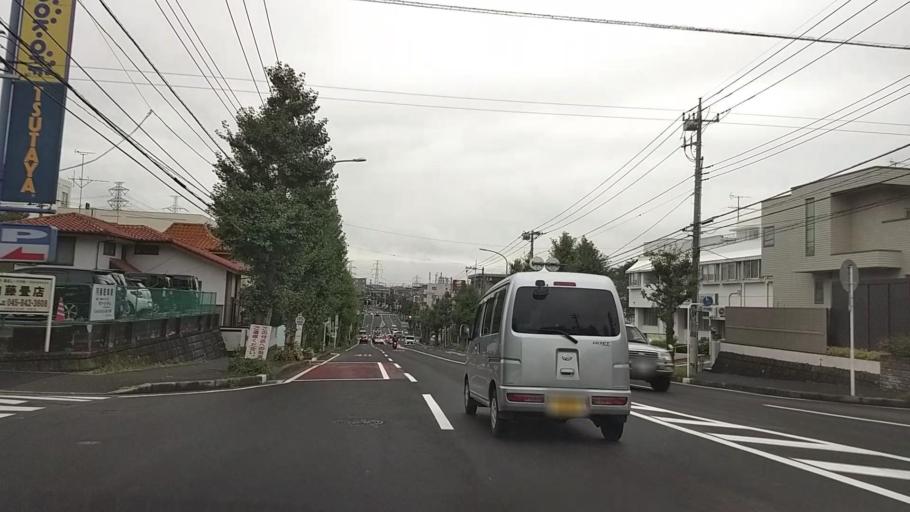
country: JP
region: Kanagawa
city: Kamakura
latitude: 35.3953
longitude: 139.5658
